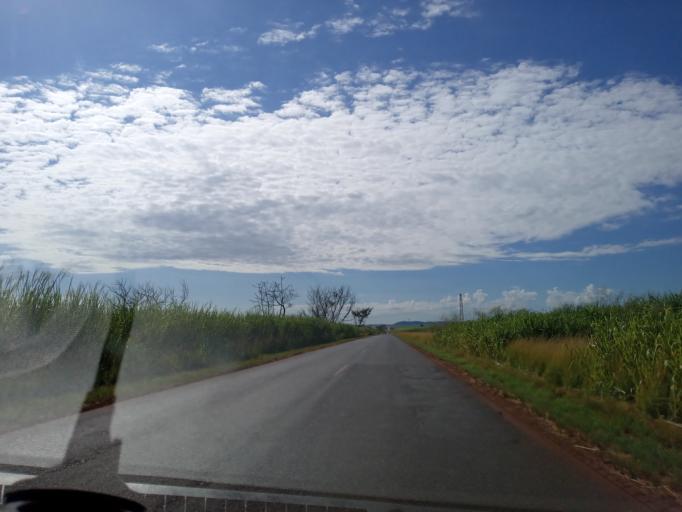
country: BR
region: Goias
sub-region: Itumbiara
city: Itumbiara
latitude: -18.4542
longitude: -49.1529
